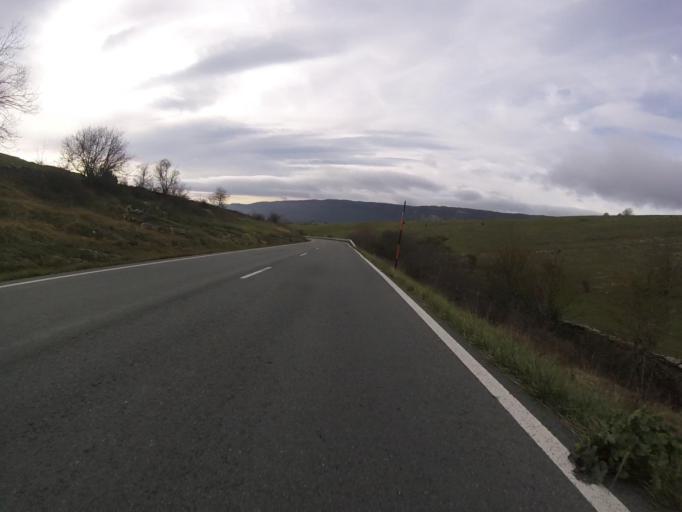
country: ES
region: Navarre
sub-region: Provincia de Navarra
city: Arbizu
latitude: 42.8514
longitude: -2.0160
